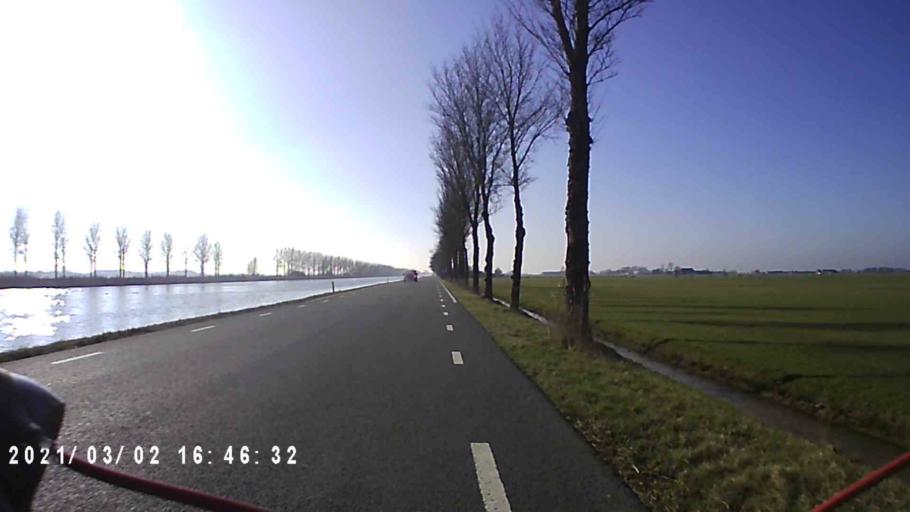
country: NL
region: Groningen
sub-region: Gemeente Zuidhorn
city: Grijpskerk
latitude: 53.2467
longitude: 6.2881
